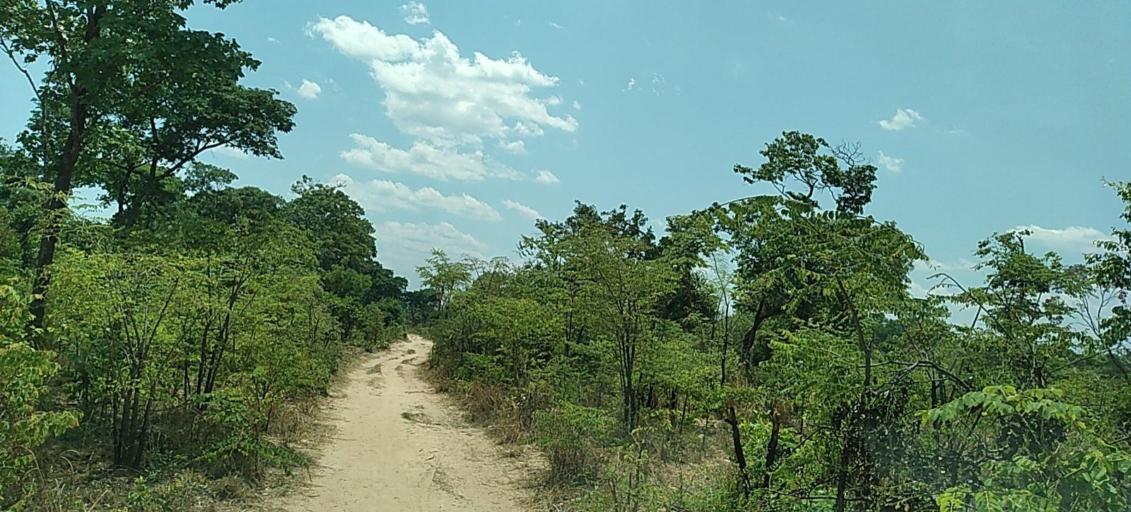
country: ZM
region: Central
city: Kapiri Mposhi
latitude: -13.6324
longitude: 28.7608
